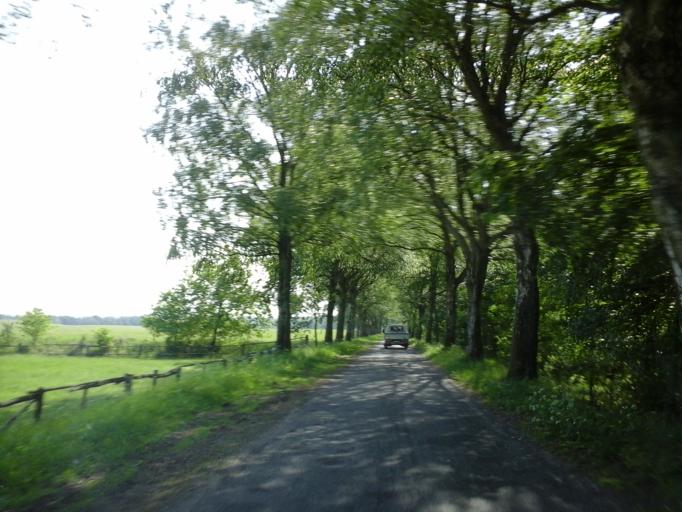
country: PL
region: West Pomeranian Voivodeship
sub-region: Powiat stargardzki
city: Dobrzany
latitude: 53.3696
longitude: 15.5029
